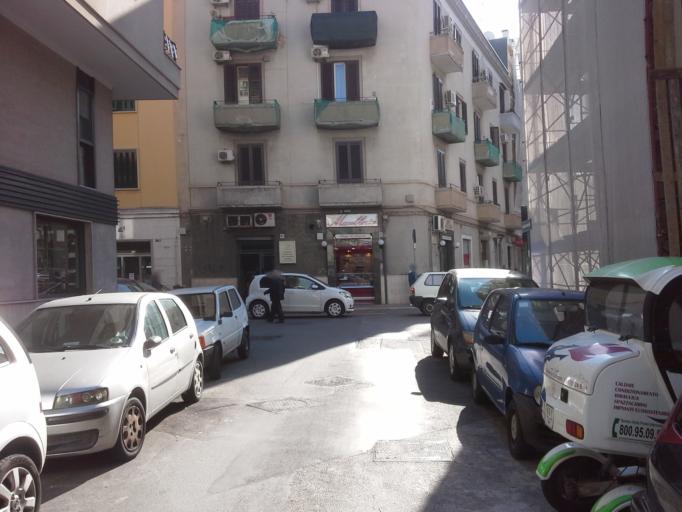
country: IT
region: Apulia
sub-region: Provincia di Bari
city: Bari
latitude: 41.1226
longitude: 16.8529
